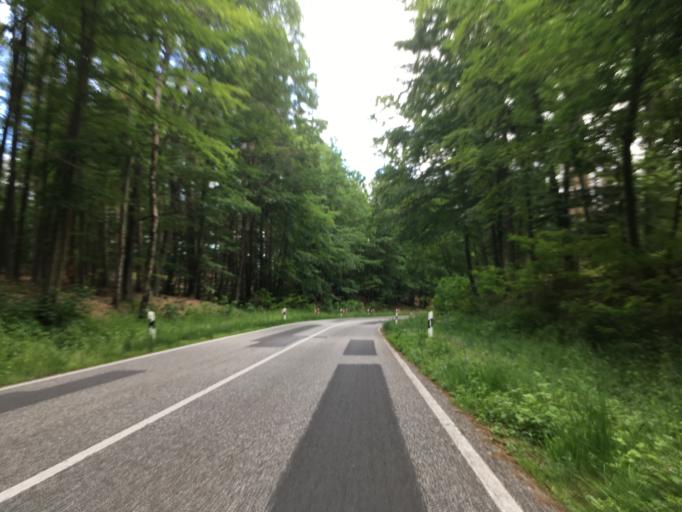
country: DE
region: Brandenburg
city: Falkenberg
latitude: 52.7499
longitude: 13.9809
